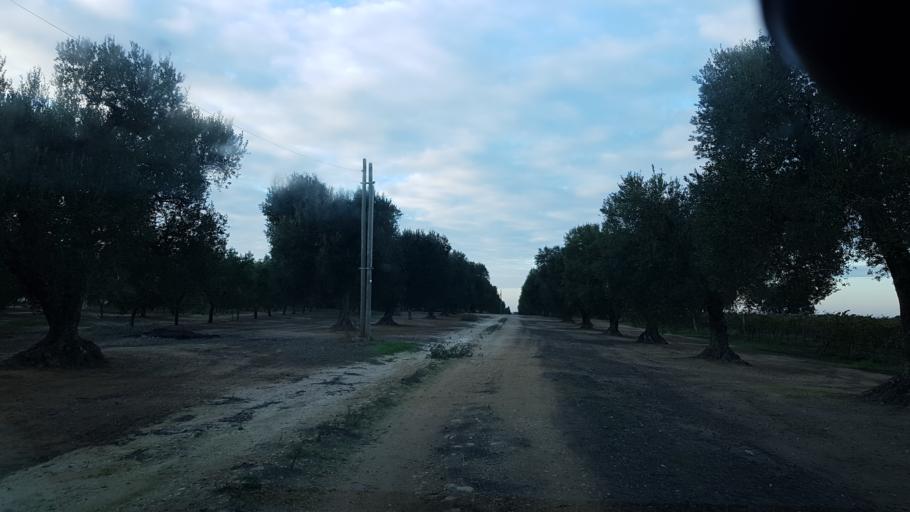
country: IT
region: Apulia
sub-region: Provincia di Brindisi
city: La Rosa
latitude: 40.5881
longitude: 17.9914
